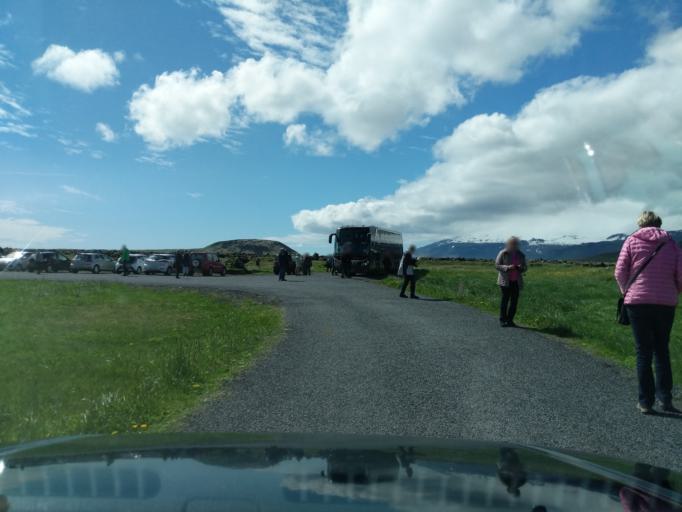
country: IS
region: West
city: Olafsvik
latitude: 64.8221
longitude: -23.3841
